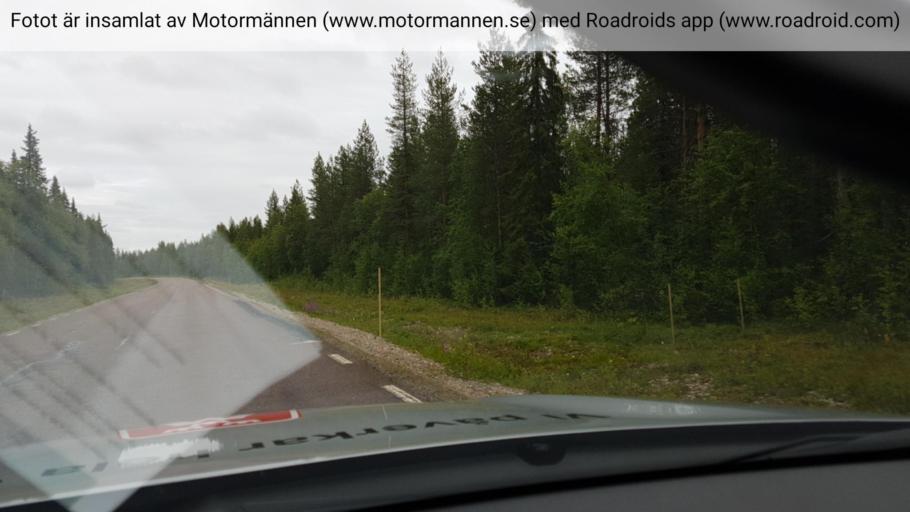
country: SE
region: Norrbotten
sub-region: Overkalix Kommun
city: OEverkalix
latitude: 67.0663
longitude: 22.3996
